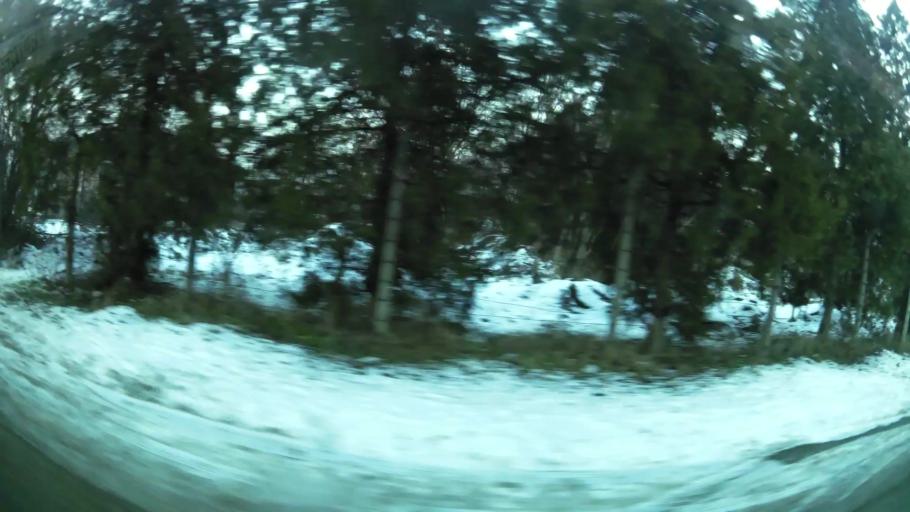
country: MK
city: Creshevo
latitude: 42.0011
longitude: 21.5030
